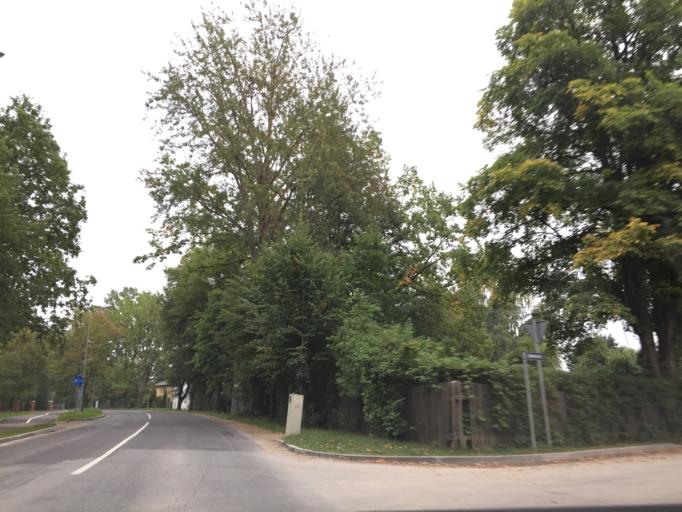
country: LV
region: Ogre
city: Ogre
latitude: 56.8126
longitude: 24.6355
